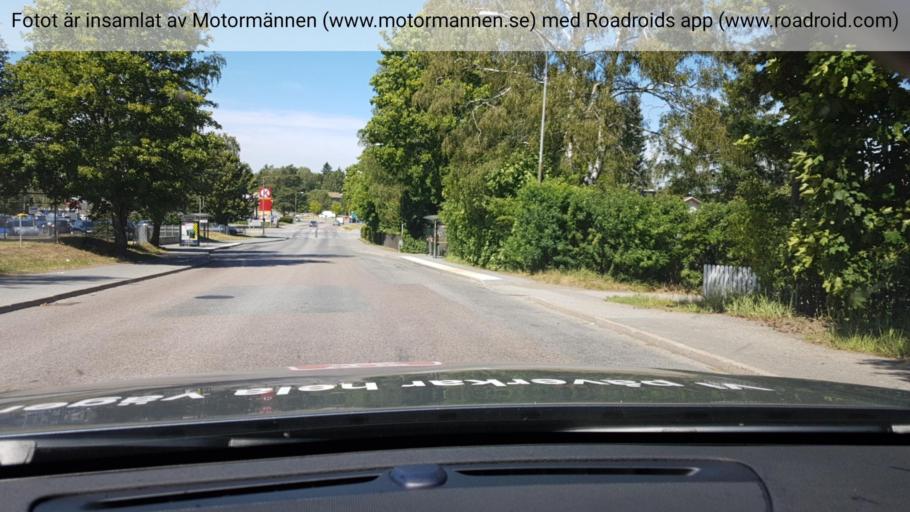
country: SE
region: Stockholm
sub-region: Haninge Kommun
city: Haninge
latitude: 59.1741
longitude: 18.1454
